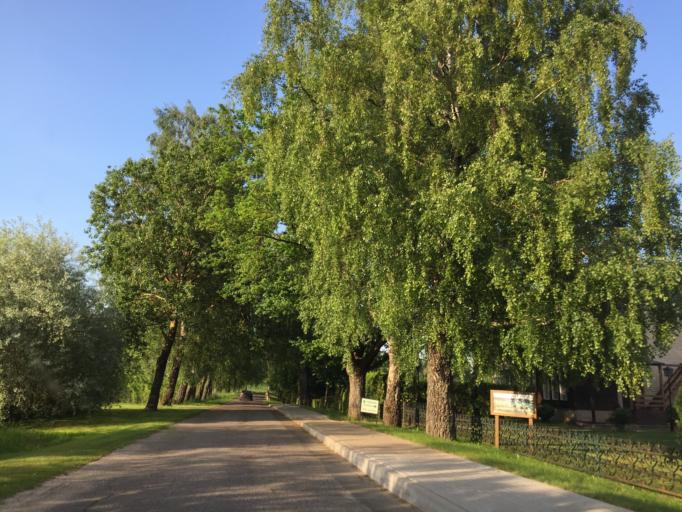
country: LT
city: Plateliai
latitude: 56.0436
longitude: 21.8223
